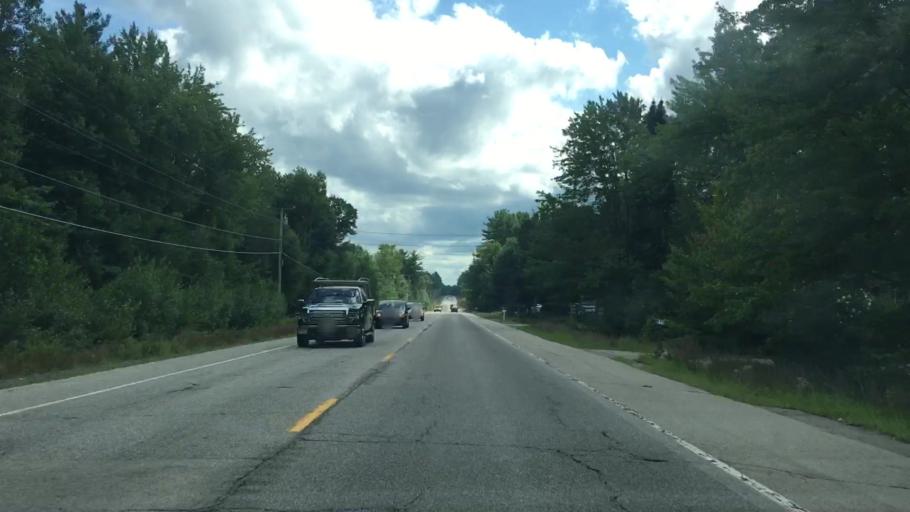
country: US
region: Maine
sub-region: York County
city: South Sanford
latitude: 43.3928
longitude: -70.7395
